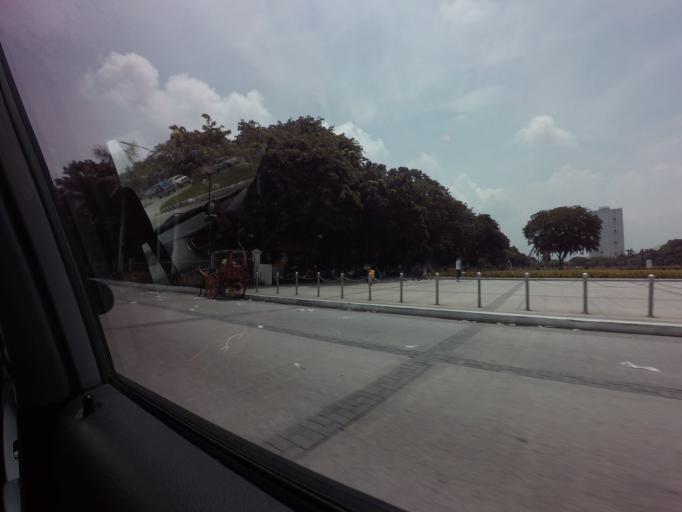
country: PH
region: Metro Manila
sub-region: City of Manila
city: Port Area
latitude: 14.5818
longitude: 120.9763
